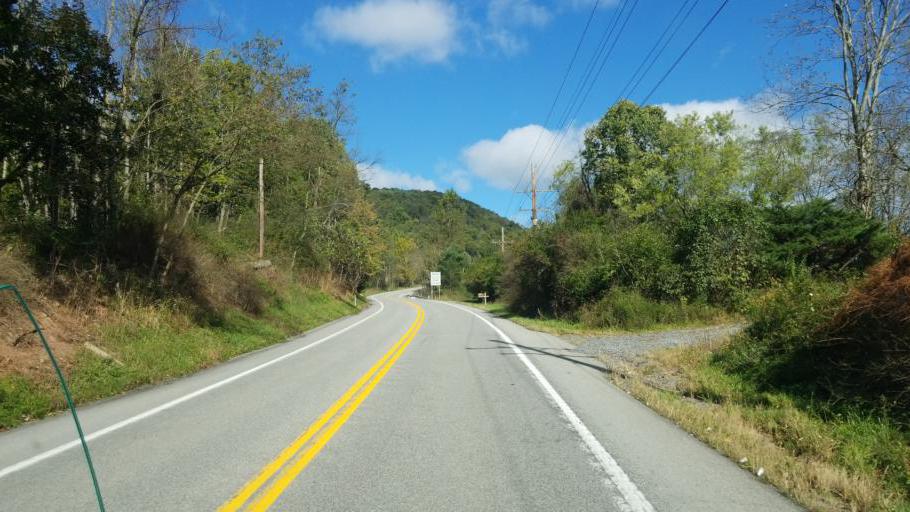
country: US
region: Pennsylvania
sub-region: Fulton County
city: McConnellsburg
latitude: 39.9590
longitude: -78.0246
